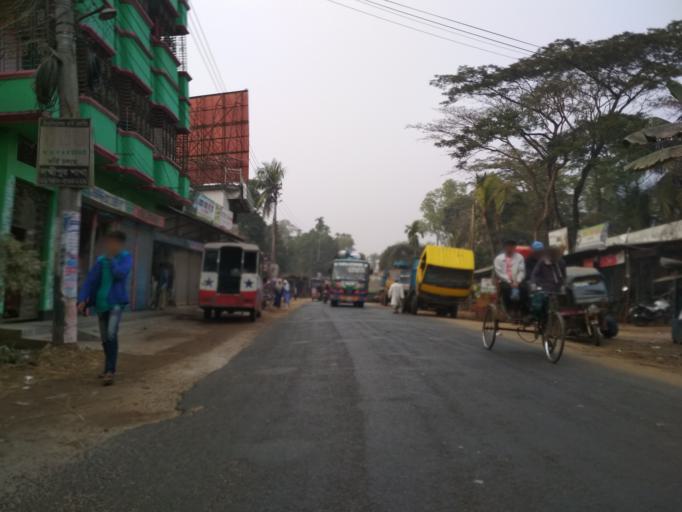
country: BD
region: Chittagong
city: Lakshmipur
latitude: 22.9293
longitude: 90.8335
